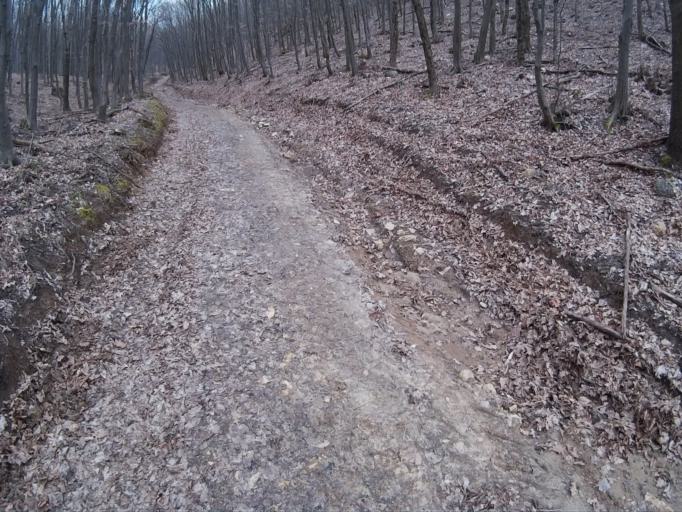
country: HU
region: Veszprem
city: Veszprem
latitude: 47.1731
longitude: 17.8707
